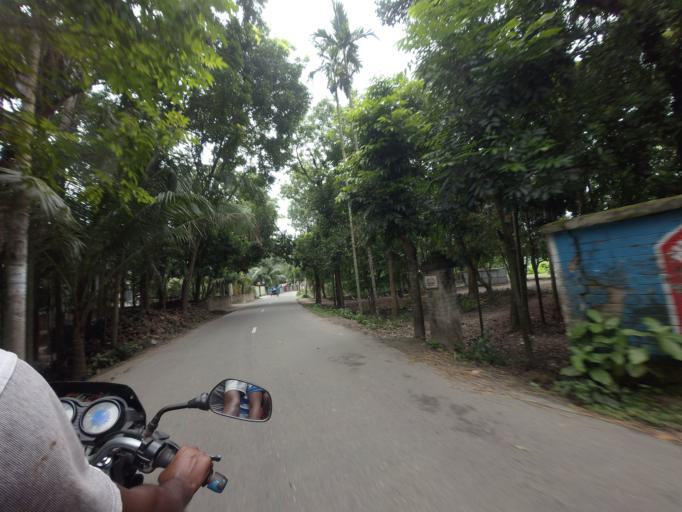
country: BD
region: Khulna
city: Kalia
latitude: 23.1772
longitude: 89.6471
